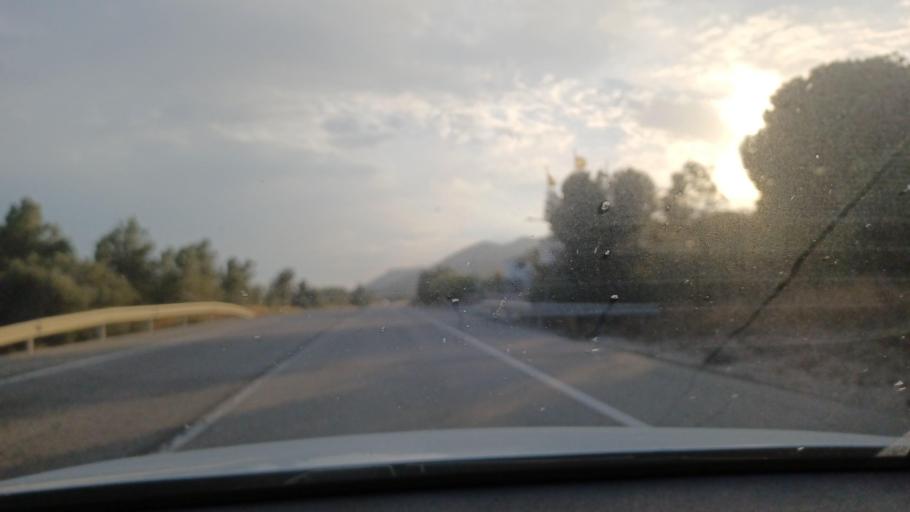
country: ES
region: Catalonia
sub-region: Provincia de Tarragona
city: Colldejou
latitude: 40.9835
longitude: 0.9032
